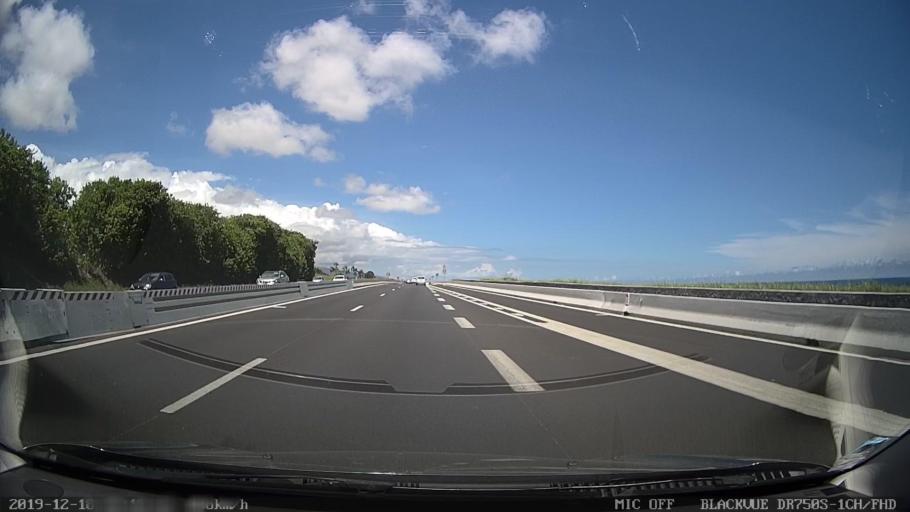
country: RE
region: Reunion
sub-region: Reunion
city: Sainte-Suzanne
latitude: -20.9007
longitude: 55.5926
